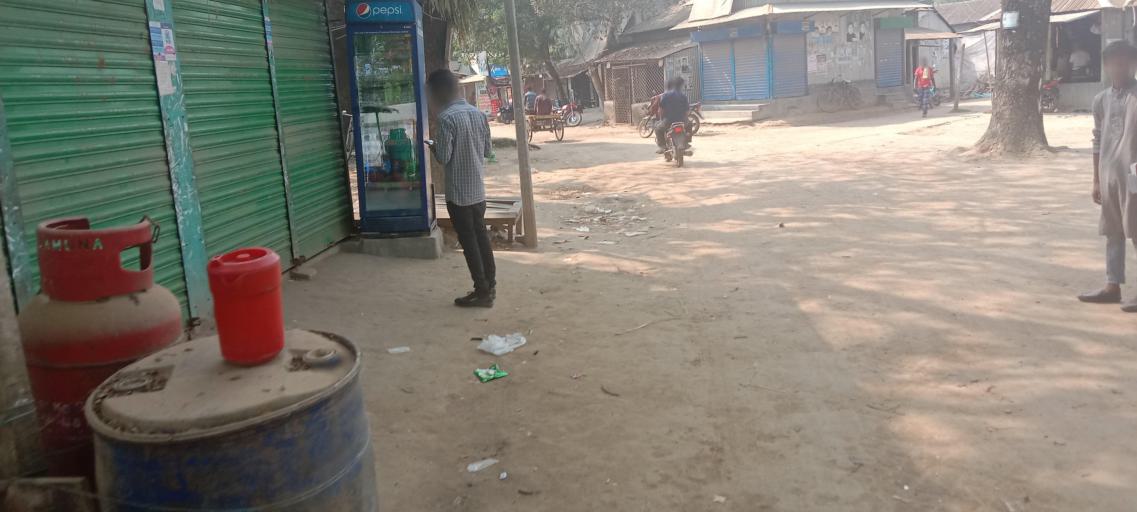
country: BD
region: Dhaka
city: Sakhipur
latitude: 24.3338
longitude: 90.2884
